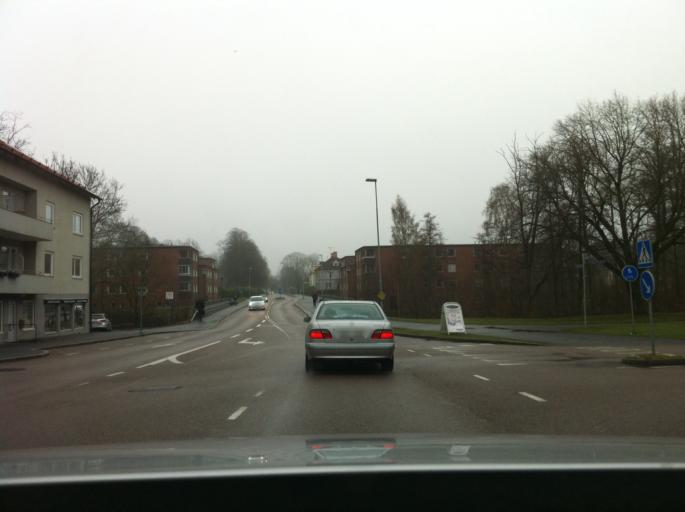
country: SE
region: Vaestra Goetaland
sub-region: Alingsas Kommun
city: Alingsas
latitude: 57.9361
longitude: 12.5322
